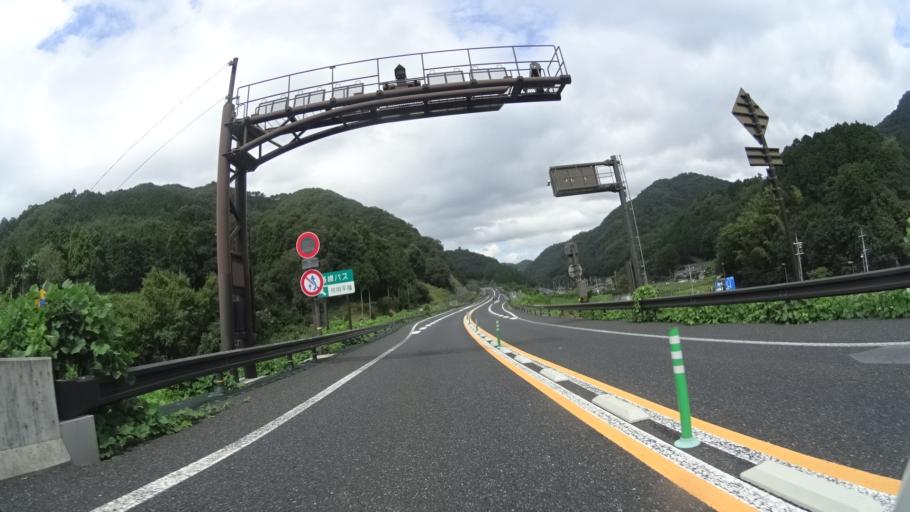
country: JP
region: Hyogo
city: Yamazakicho-nakabirose
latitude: 35.0571
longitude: 134.3661
